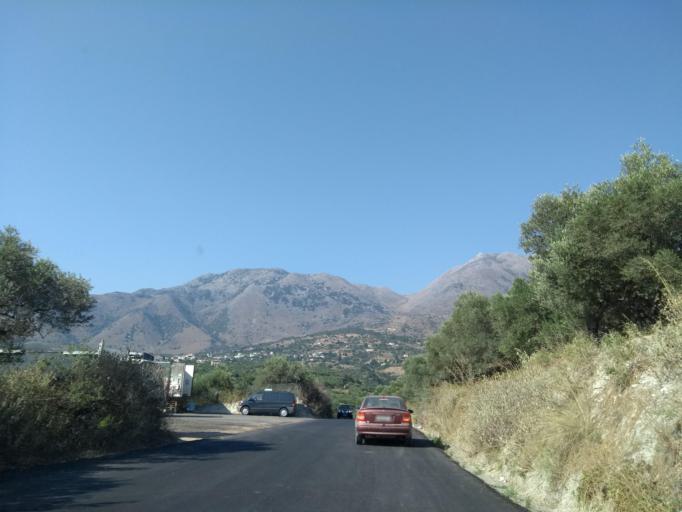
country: GR
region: Crete
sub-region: Nomos Chanias
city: Georgioupolis
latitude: 35.3301
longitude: 24.3008
